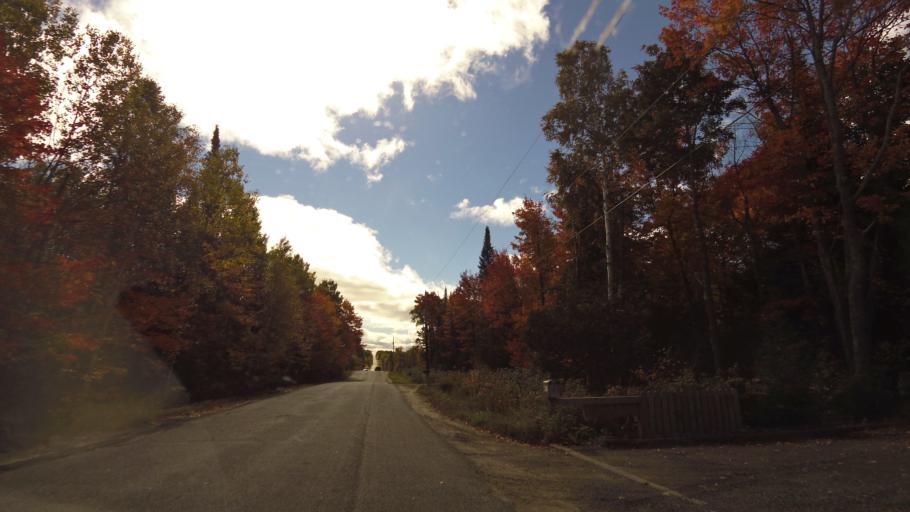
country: CA
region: Ontario
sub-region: Nipissing District
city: North Bay
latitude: 46.3705
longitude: -79.4872
